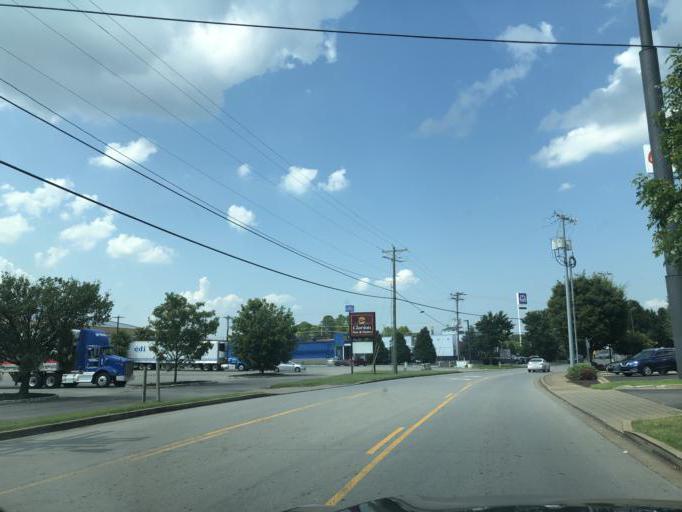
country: US
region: Tennessee
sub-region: Rutherford County
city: Murfreesboro
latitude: 35.8455
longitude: -86.4308
